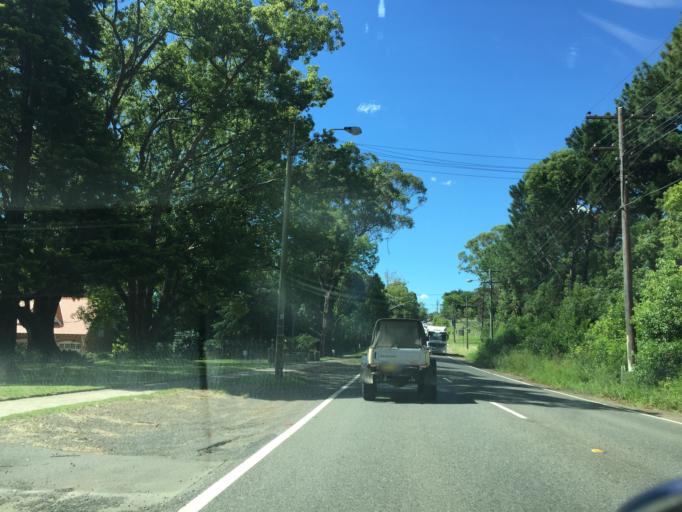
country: AU
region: New South Wales
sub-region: The Hills Shire
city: Glenhaven
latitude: -33.7014
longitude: 151.0151
